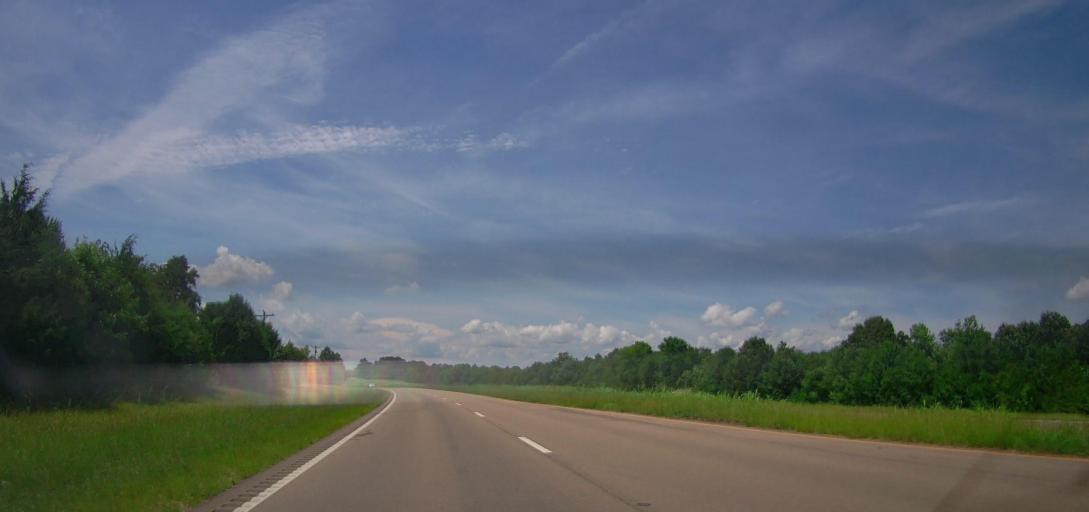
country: US
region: Mississippi
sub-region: Monroe County
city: Amory
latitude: 33.9522
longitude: -88.6042
